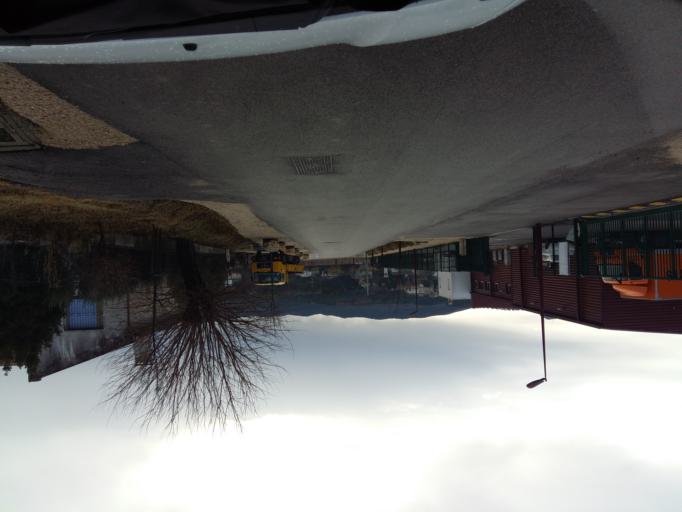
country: FR
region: Provence-Alpes-Cote d'Azur
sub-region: Departement du Vaucluse
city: Sablet
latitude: 44.1962
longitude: 4.9967
